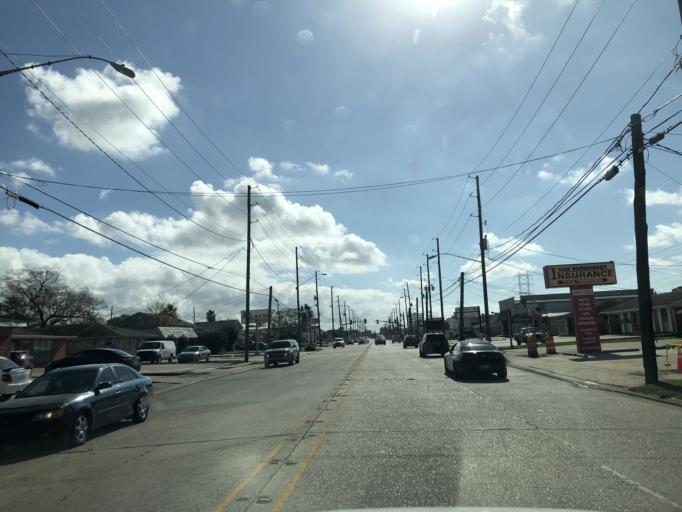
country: US
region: Louisiana
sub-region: Jefferson Parish
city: Kenner
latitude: 30.0033
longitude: -90.2201
